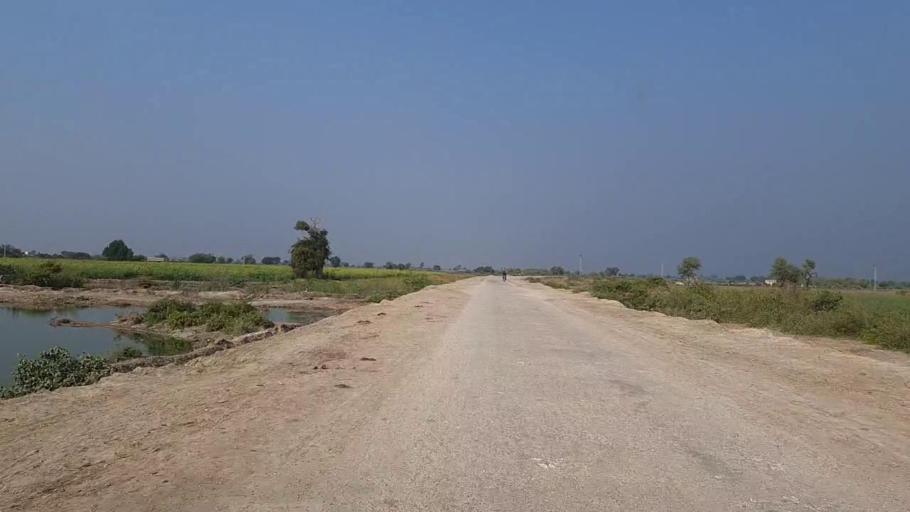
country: PK
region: Sindh
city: Mirwah Gorchani
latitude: 25.4063
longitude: 69.1408
